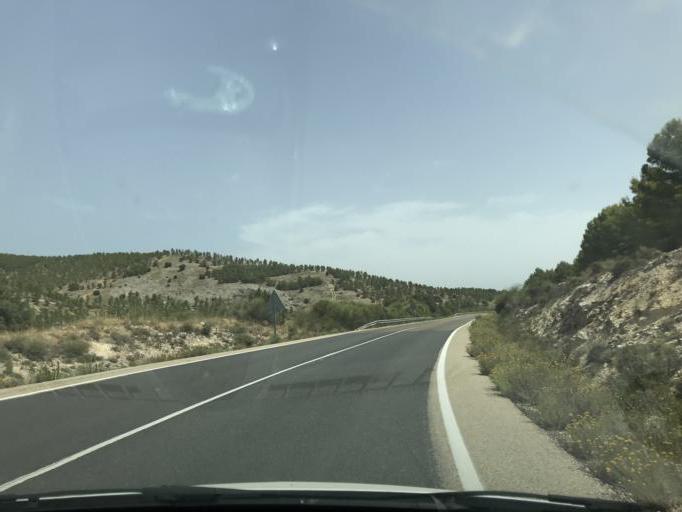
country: ES
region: Castille-La Mancha
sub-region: Provincia de Cuenca
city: Albalate de las Nogueras
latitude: 40.3891
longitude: -2.2698
